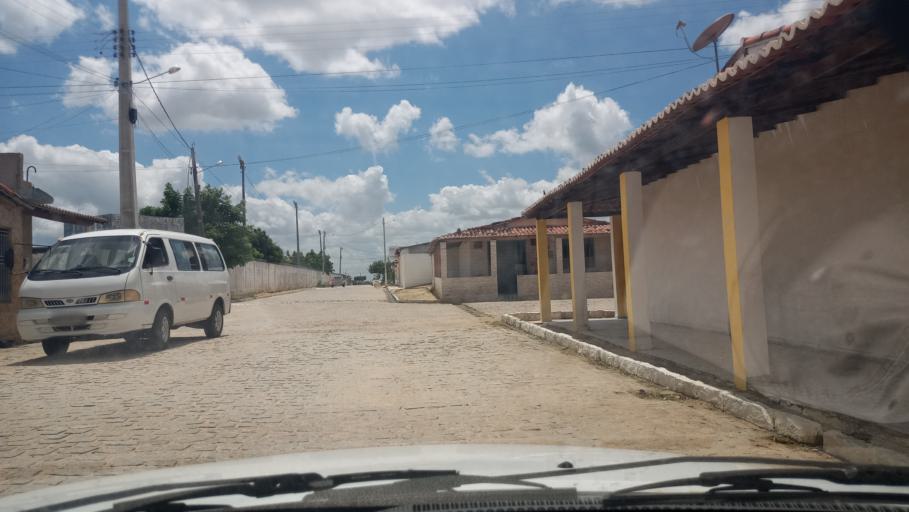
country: BR
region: Rio Grande do Norte
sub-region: Nova Cruz
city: Nova Cruz
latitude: -6.4588
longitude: -35.5798
